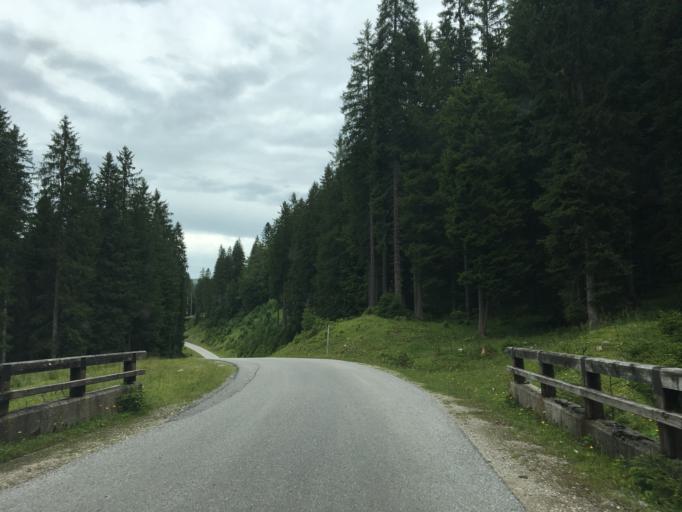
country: AT
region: Salzburg
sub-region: Politischer Bezirk Salzburg-Umgebung
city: Strobl
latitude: 47.6384
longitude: 13.4189
